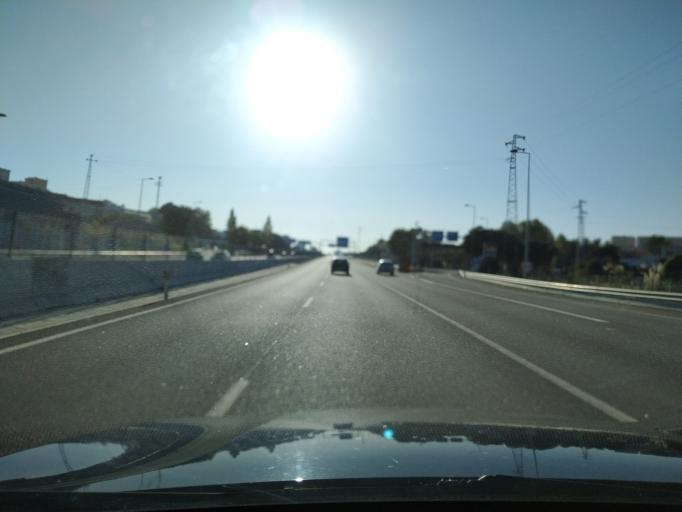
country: PT
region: Porto
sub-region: Vila Nova de Gaia
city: Vilar de Andorinho
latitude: 41.1026
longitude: -8.6009
